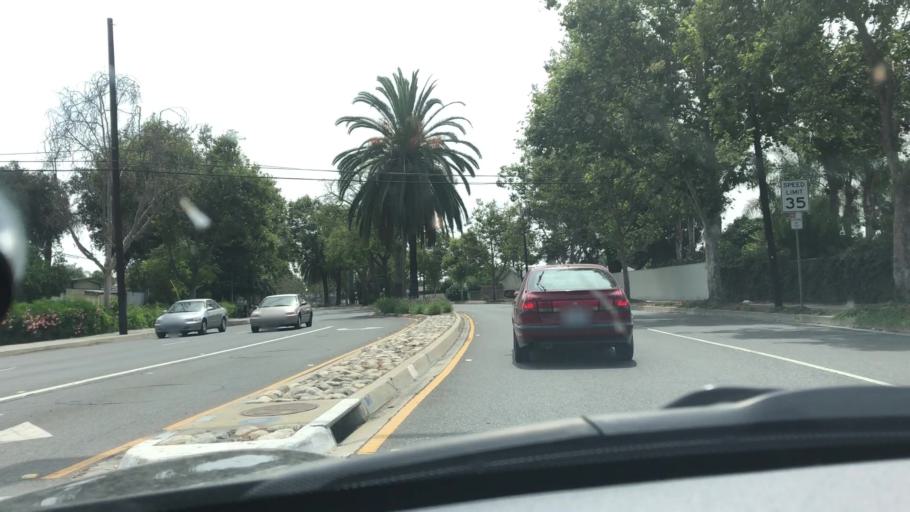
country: US
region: California
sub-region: Los Angeles County
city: Pomona
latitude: 34.0334
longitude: -117.7535
